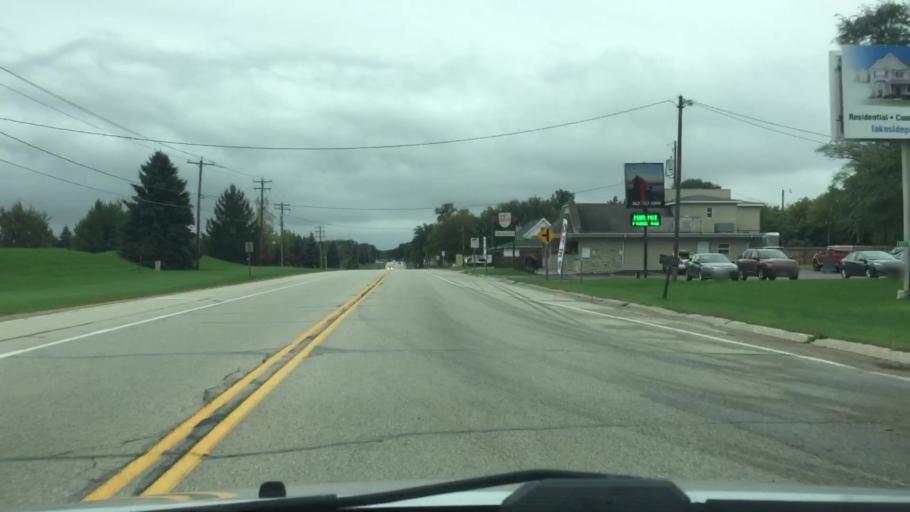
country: US
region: Wisconsin
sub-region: Walworth County
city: Elkhorn
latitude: 42.7492
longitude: -88.5535
